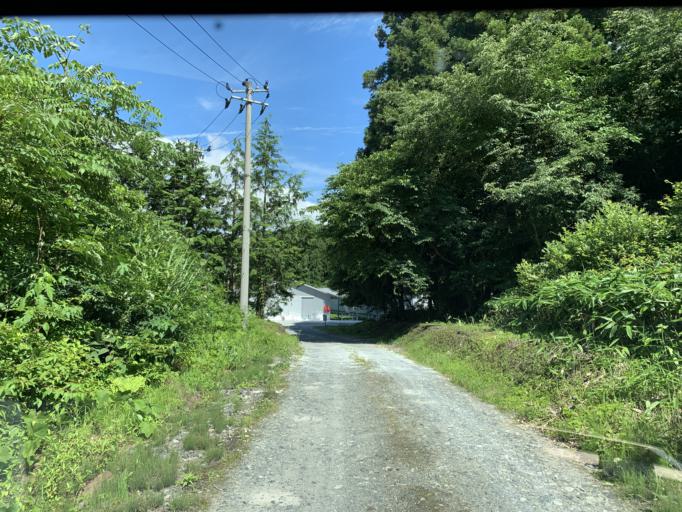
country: JP
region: Iwate
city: Ichinoseki
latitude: 38.9683
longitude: 140.9523
